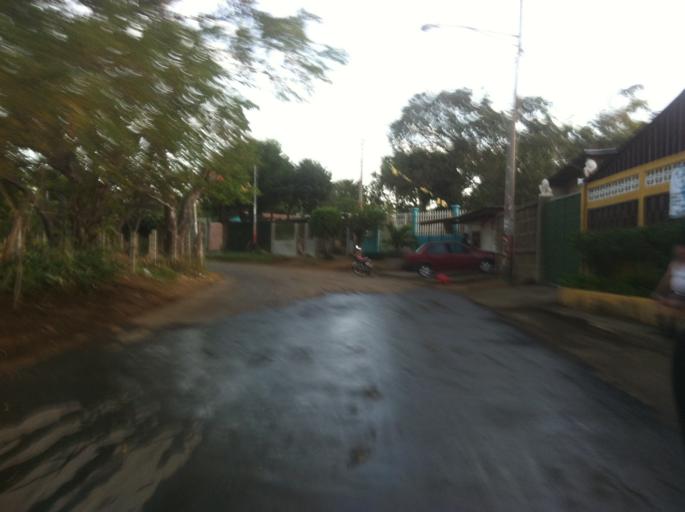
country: NI
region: Managua
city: Ciudad Sandino
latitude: 12.0760
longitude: -86.3279
